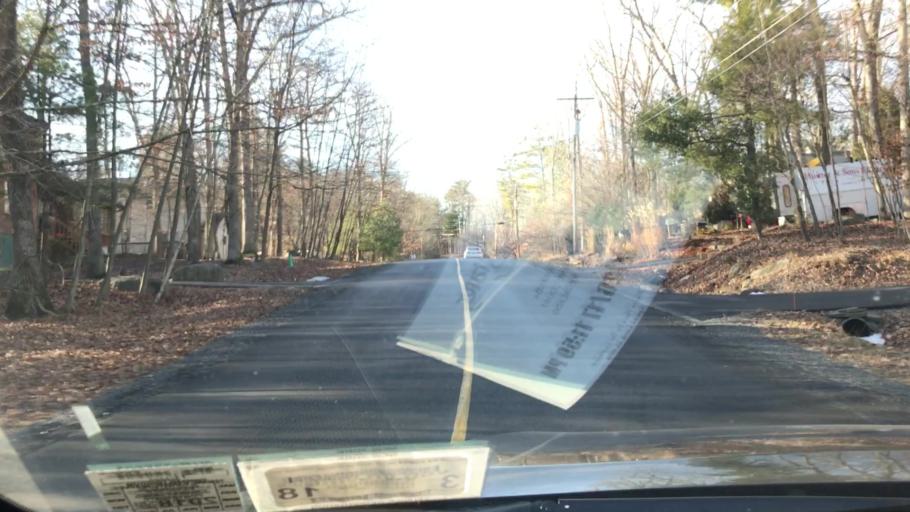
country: US
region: Pennsylvania
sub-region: Monroe County
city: Arlington Heights
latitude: 41.0425
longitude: -75.2340
